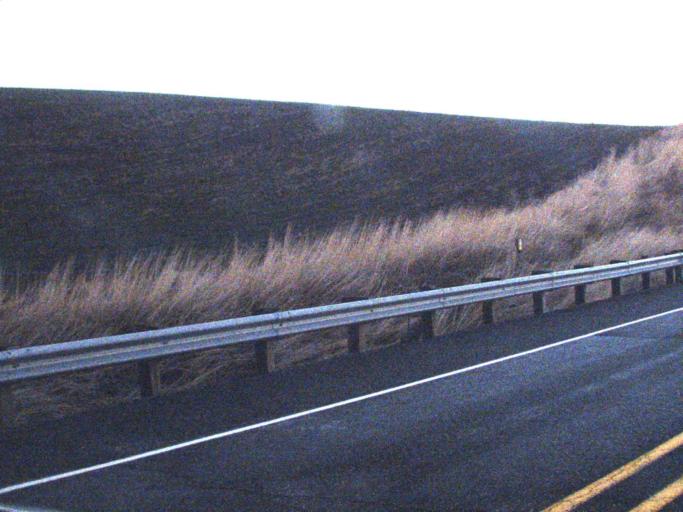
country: US
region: Washington
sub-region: Garfield County
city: Pomeroy
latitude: 46.5848
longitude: -117.7778
